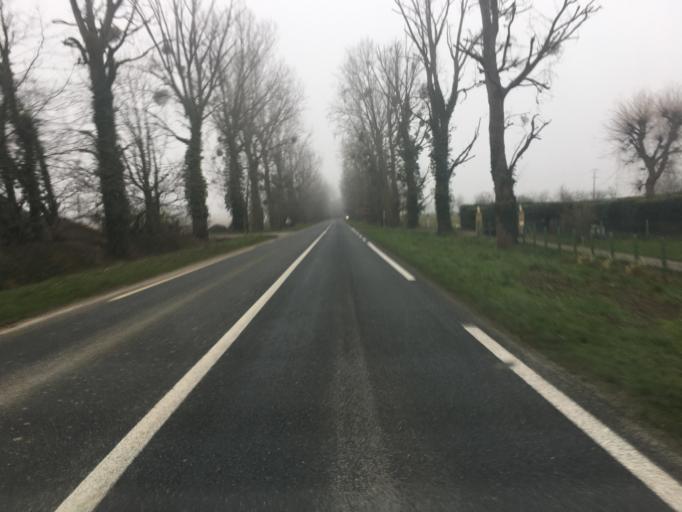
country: FR
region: Haute-Normandie
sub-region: Departement de la Seine-Maritime
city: La Remuee
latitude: 49.5272
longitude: 0.4208
